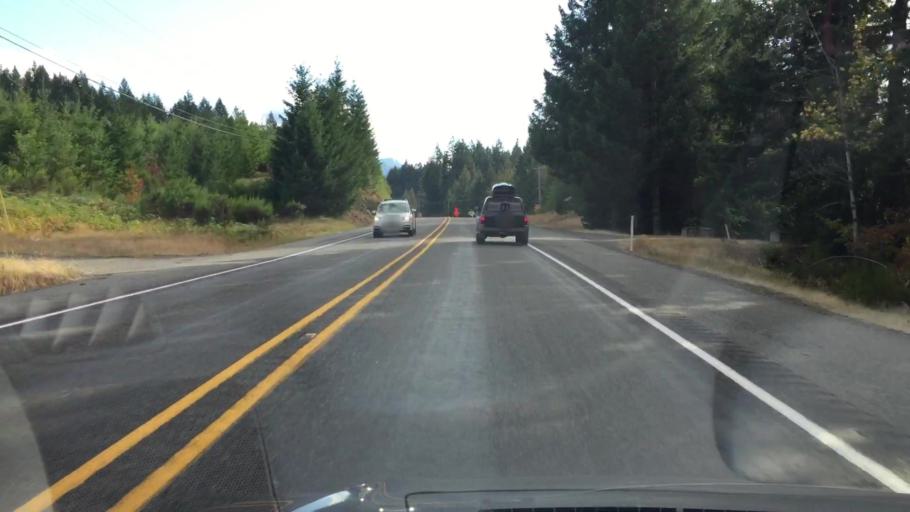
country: US
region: Washington
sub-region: Lewis County
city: Morton
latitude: 46.6214
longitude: -121.6610
